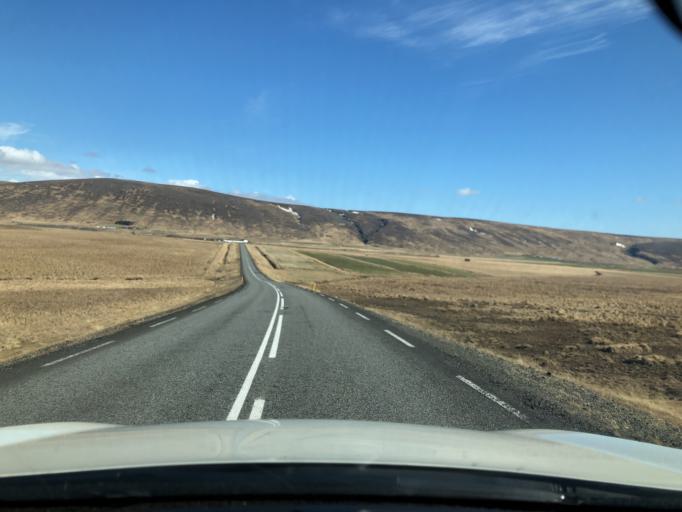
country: IS
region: South
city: Hveragerdi
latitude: 64.6844
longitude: -21.2406
